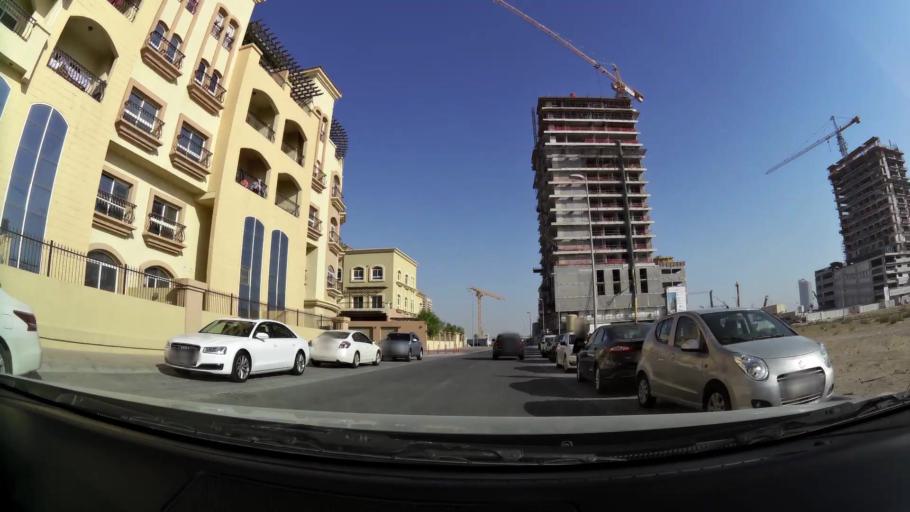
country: AE
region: Dubai
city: Dubai
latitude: 25.0620
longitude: 55.2172
